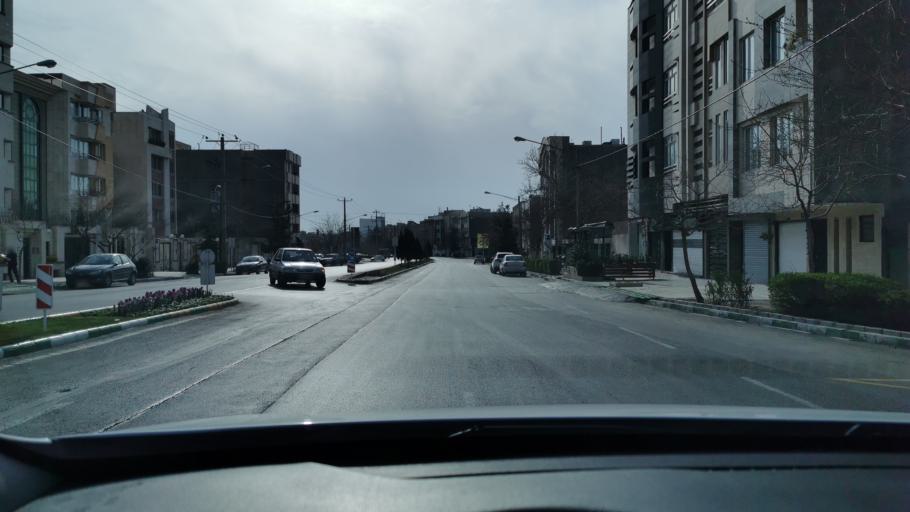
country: IR
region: Razavi Khorasan
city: Mashhad
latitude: 36.3149
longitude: 59.5105
